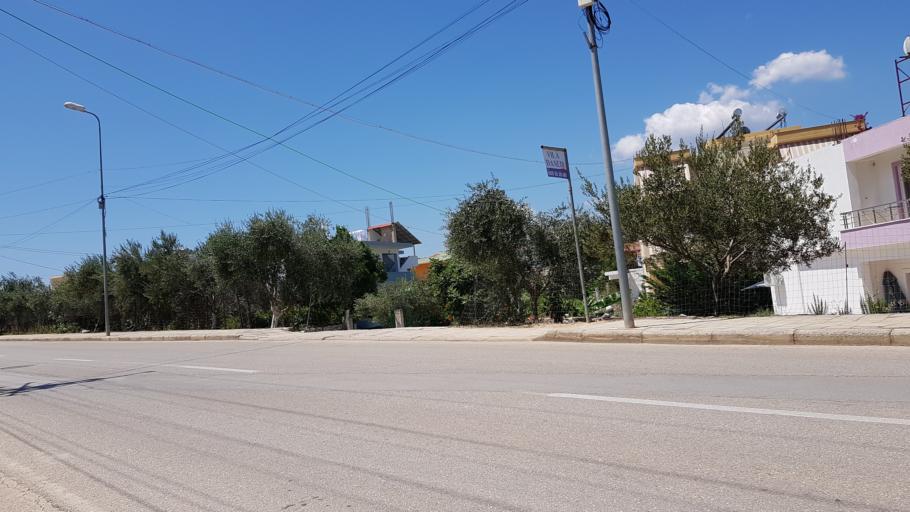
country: AL
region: Vlore
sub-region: Rrethi i Sarandes
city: Xarre
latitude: 39.7657
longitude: 20.0017
